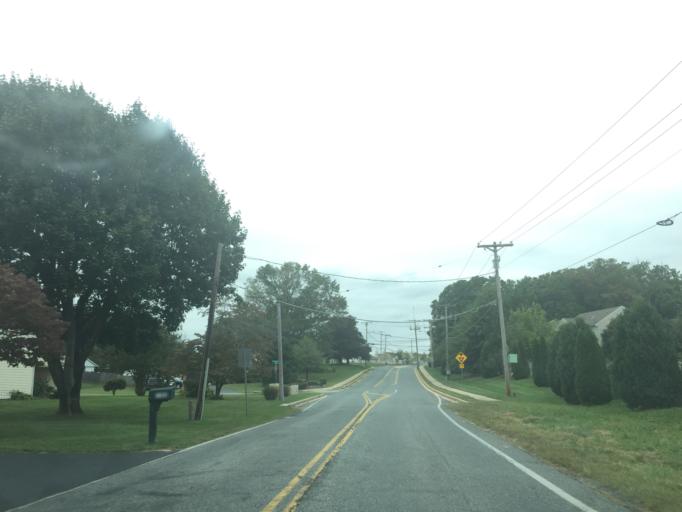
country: US
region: Maryland
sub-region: Harford County
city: Bel Air South
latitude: 39.5074
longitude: -76.3440
